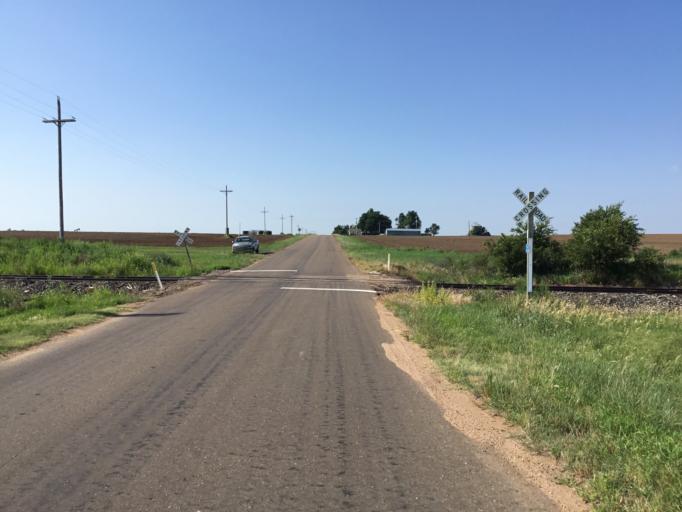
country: US
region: Kansas
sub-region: Pratt County
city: Pratt
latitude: 37.5100
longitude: -98.7389
